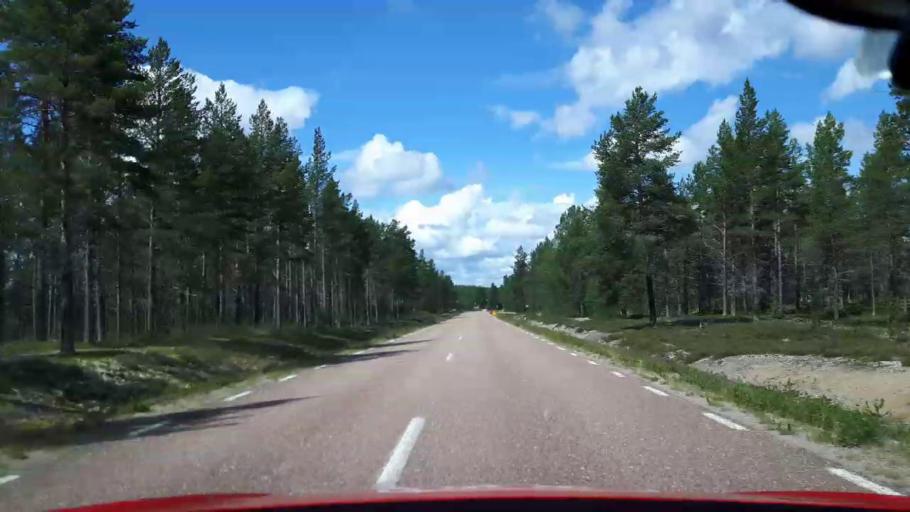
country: SE
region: Dalarna
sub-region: Alvdalens Kommun
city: AElvdalen
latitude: 61.8202
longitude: 13.5757
